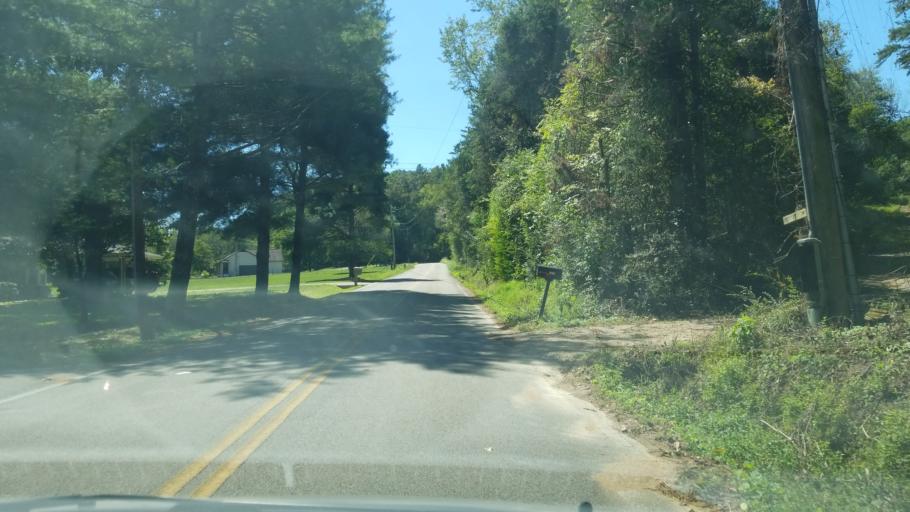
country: US
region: Tennessee
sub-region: Hamilton County
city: Harrison
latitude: 35.1077
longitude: -85.0852
